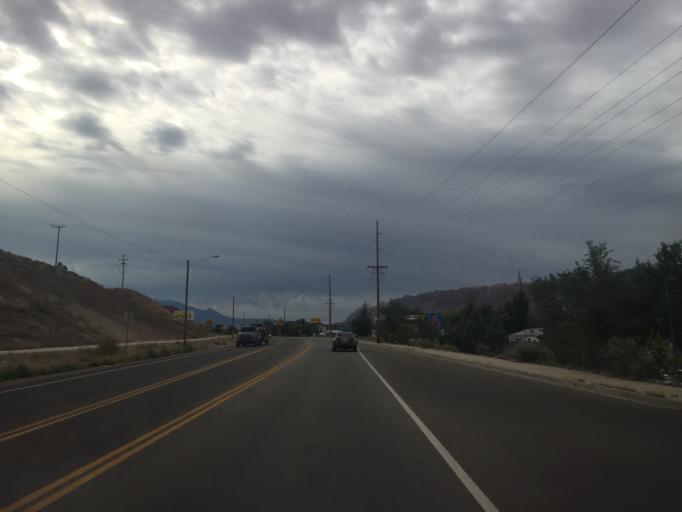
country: US
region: Utah
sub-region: Grand County
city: Moab
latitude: 38.5903
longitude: -109.5626
